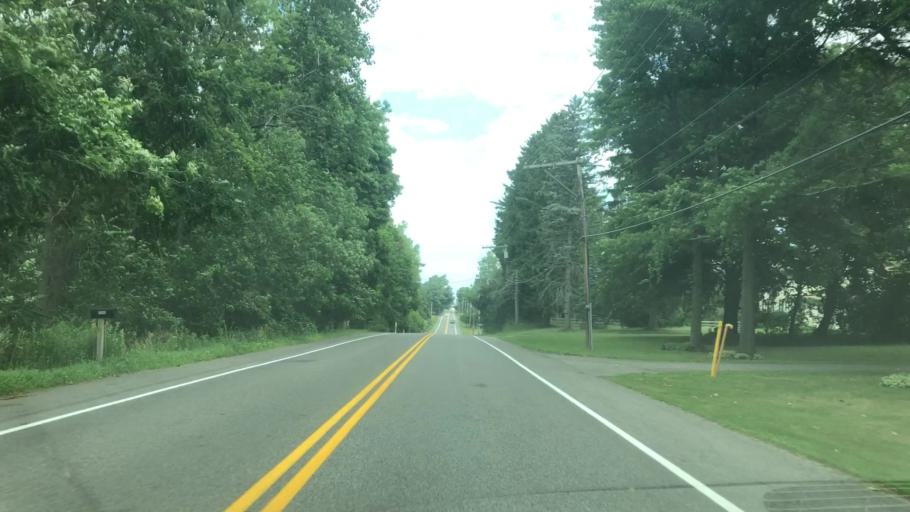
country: US
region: New York
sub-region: Monroe County
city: Fairport
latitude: 43.1327
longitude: -77.4005
